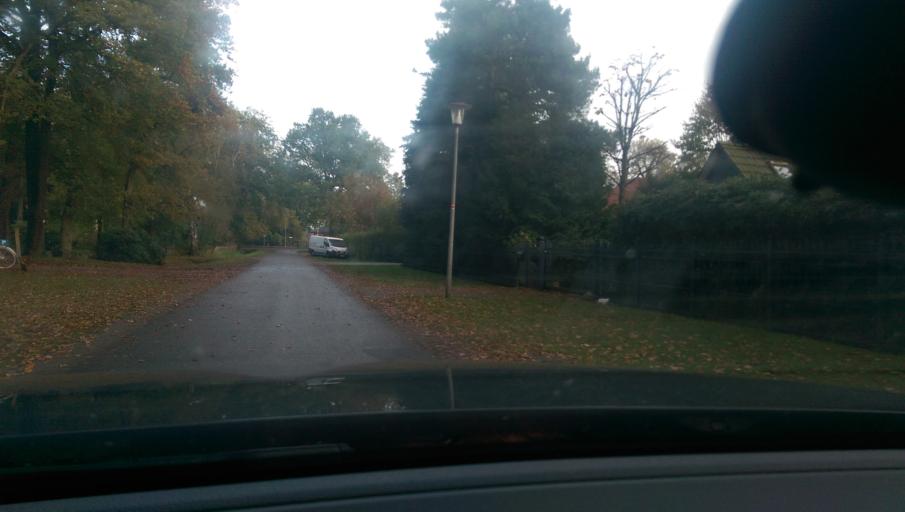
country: DE
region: Lower Saxony
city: Hellwege
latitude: 53.0728
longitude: 9.2295
